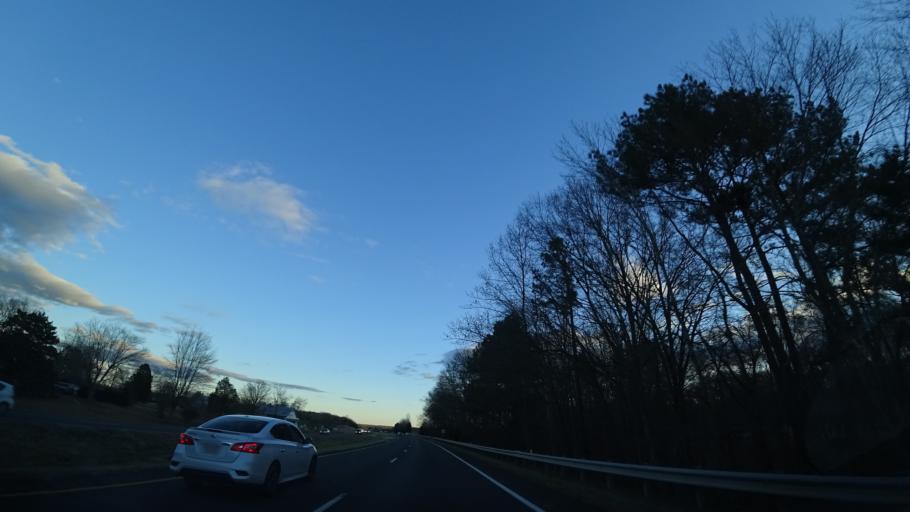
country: US
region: Virginia
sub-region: Fauquier County
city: Bealeton
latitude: 38.4471
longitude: -77.6539
